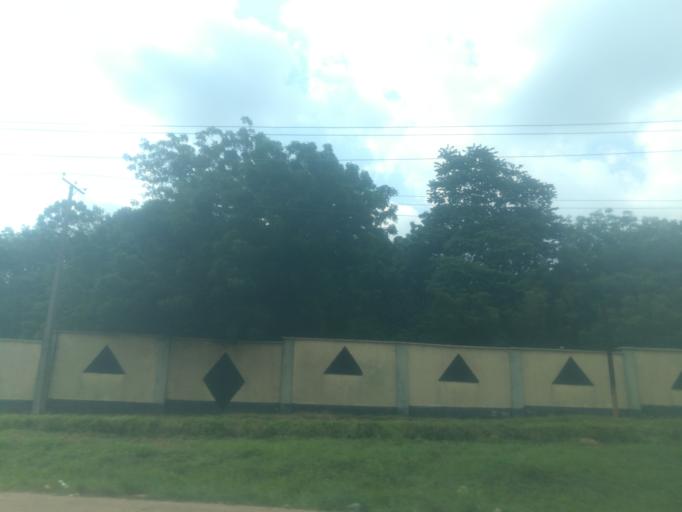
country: NG
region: Ogun
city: Abeokuta
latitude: 7.1298
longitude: 3.3018
